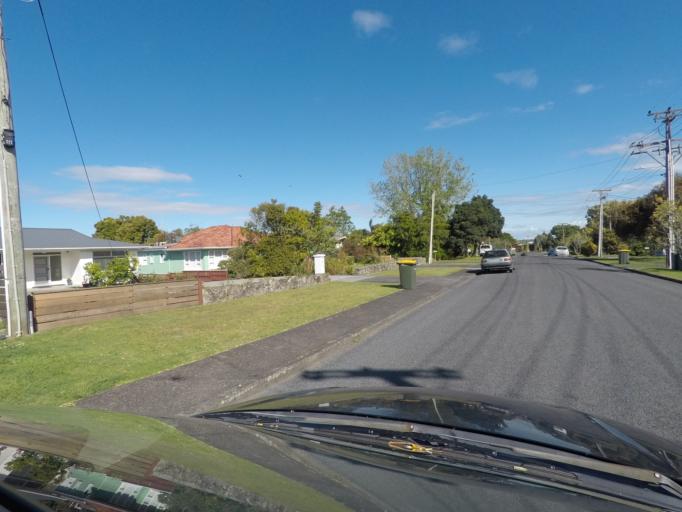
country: NZ
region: Auckland
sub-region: Auckland
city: Rosebank
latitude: -36.8615
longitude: 174.6544
